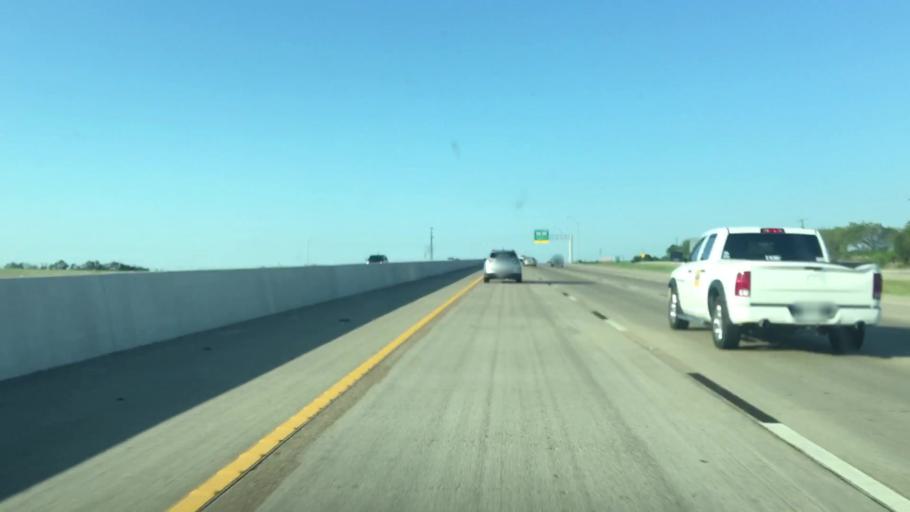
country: US
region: Texas
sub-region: McLennan County
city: Hewitt
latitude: 31.4447
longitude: -97.1799
